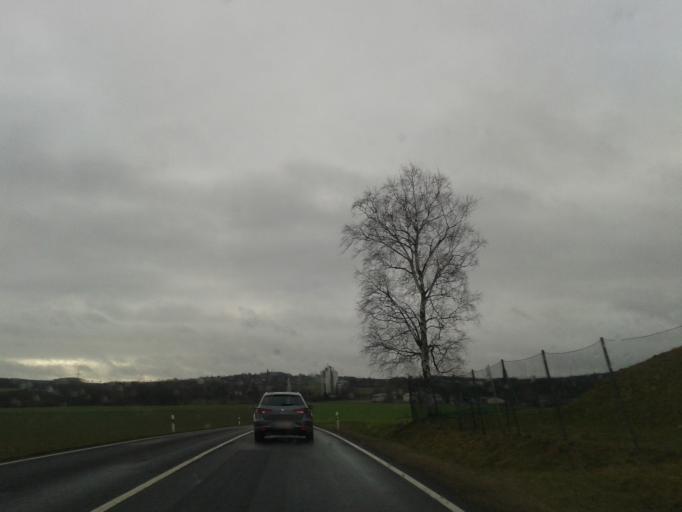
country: DE
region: Saxony
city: Grossschweidnitz
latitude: 51.0605
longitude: 14.6444
